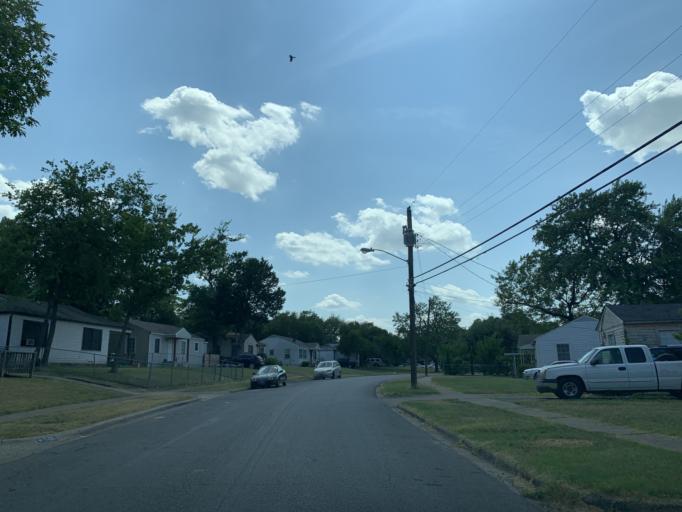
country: US
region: Texas
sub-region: Dallas County
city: Dallas
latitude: 32.7130
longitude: -96.7859
